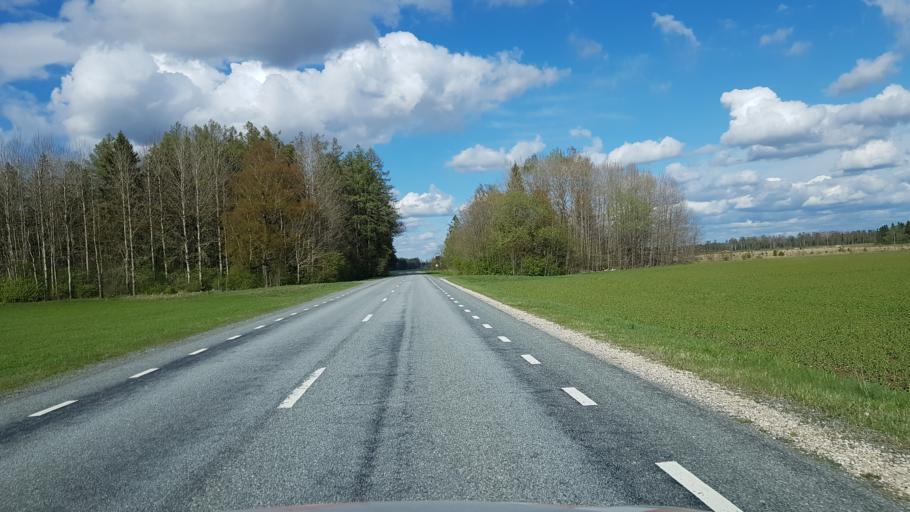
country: EE
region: Jaervamaa
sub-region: Jaerva-Jaani vald
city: Jarva-Jaani
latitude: 59.0870
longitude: 25.9727
